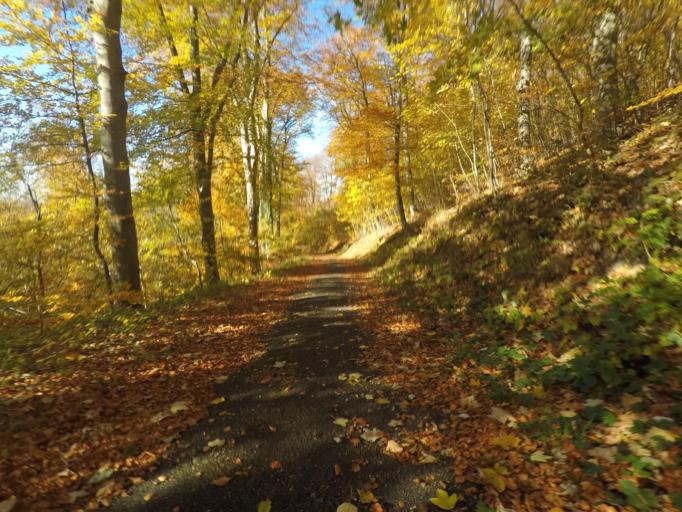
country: DE
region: Baden-Wuerttemberg
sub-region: Tuebingen Region
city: Pfullingen
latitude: 48.4389
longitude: 9.2182
